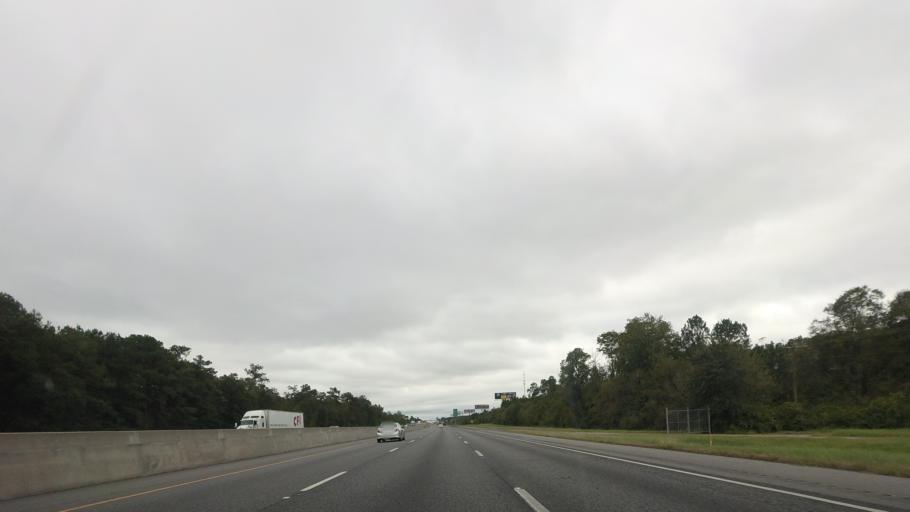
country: US
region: Georgia
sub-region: Lowndes County
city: Hahira
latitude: 31.0047
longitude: -83.3919
